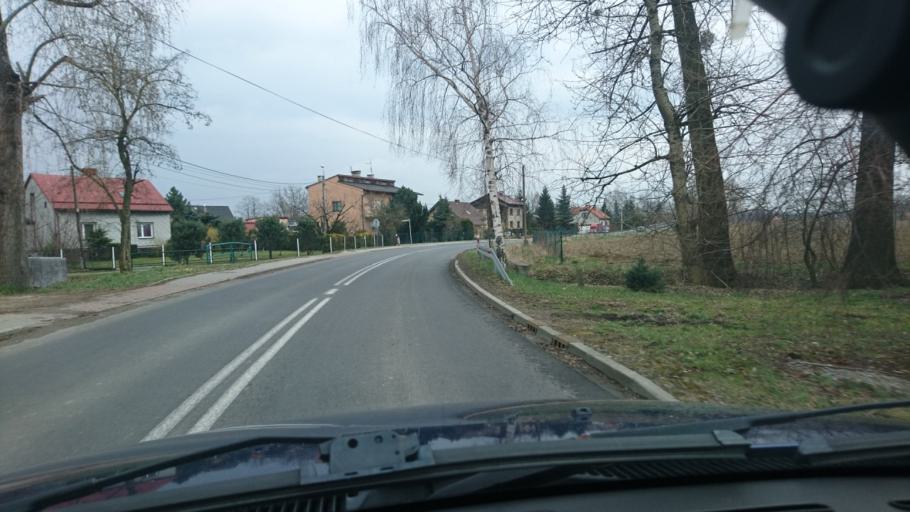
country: PL
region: Silesian Voivodeship
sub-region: Powiat bielski
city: Ligota
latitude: 49.8763
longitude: 18.9530
